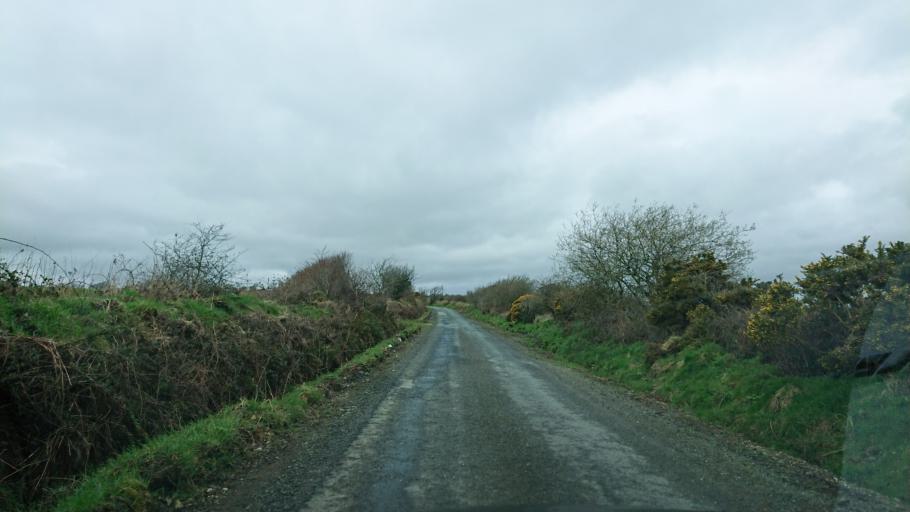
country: IE
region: Munster
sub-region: Waterford
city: Dunmore East
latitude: 52.1698
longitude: -7.0424
